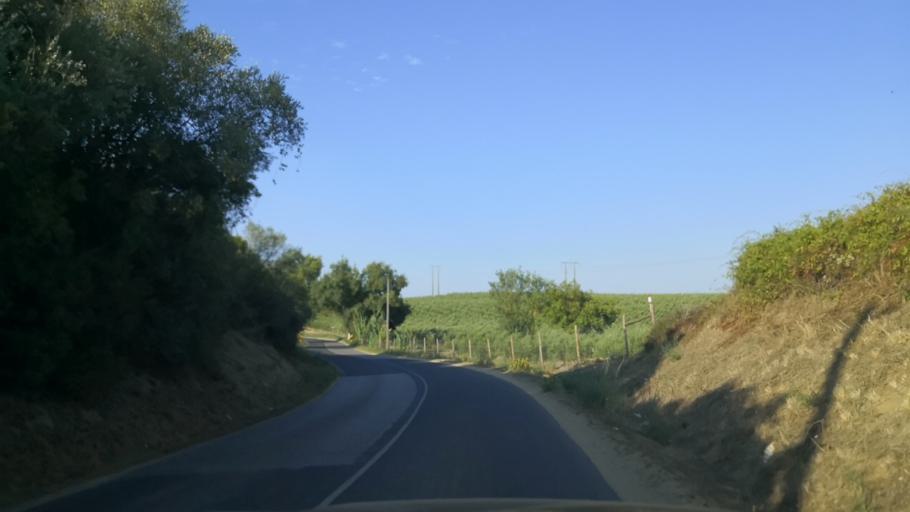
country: PT
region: Santarem
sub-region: Santarem
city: Santarem
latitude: 39.2724
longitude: -8.6630
